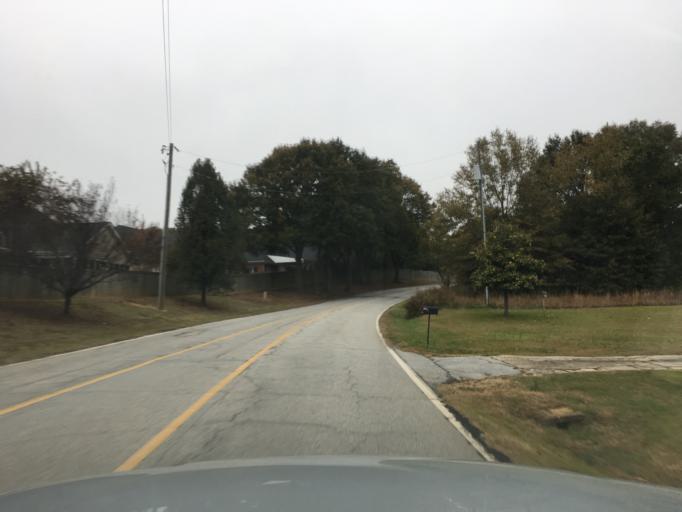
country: US
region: South Carolina
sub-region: Greenville County
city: Five Forks
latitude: 34.8273
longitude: -82.2706
